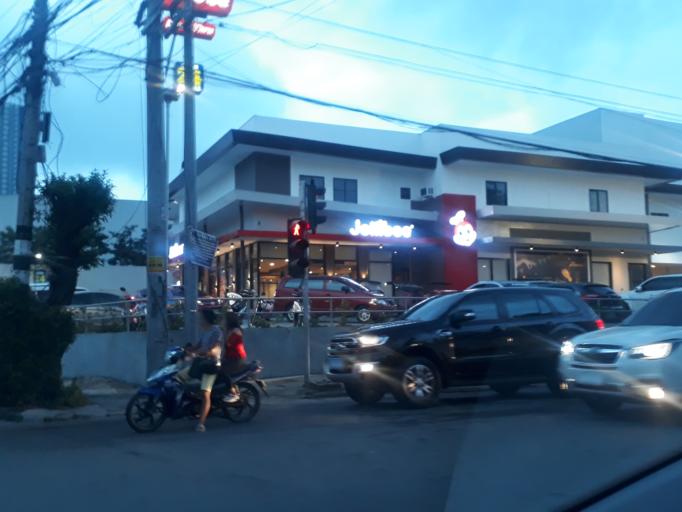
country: PH
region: Calabarzon
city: Del Monte
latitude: 14.6203
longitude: 121.0043
